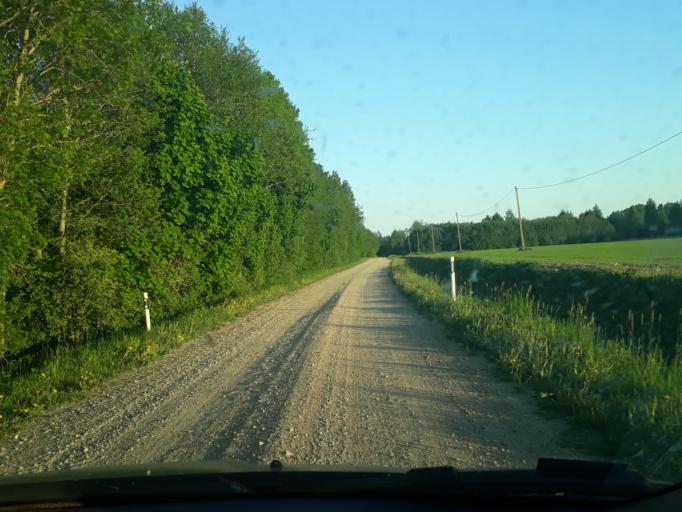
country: EE
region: Paernumaa
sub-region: Vaendra vald (alev)
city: Vandra
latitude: 58.5703
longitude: 24.9457
